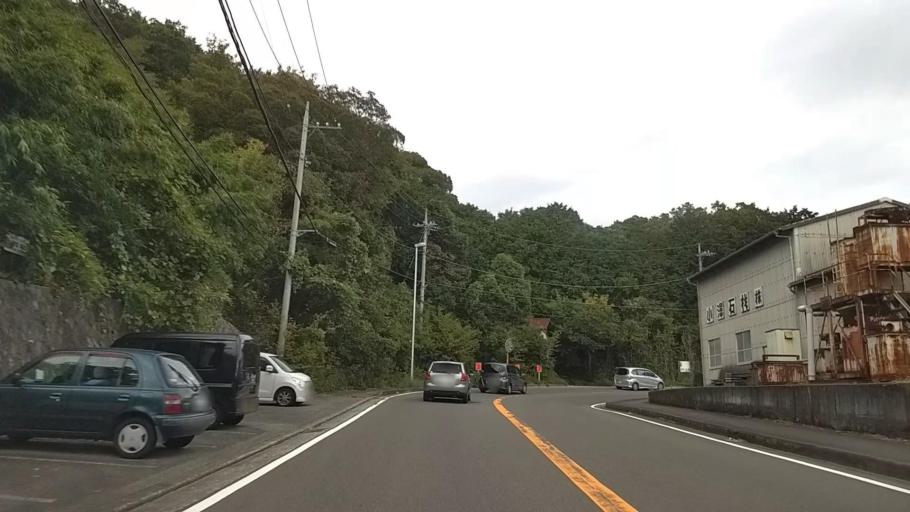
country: JP
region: Kanagawa
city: Yugawara
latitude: 35.1619
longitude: 139.1329
